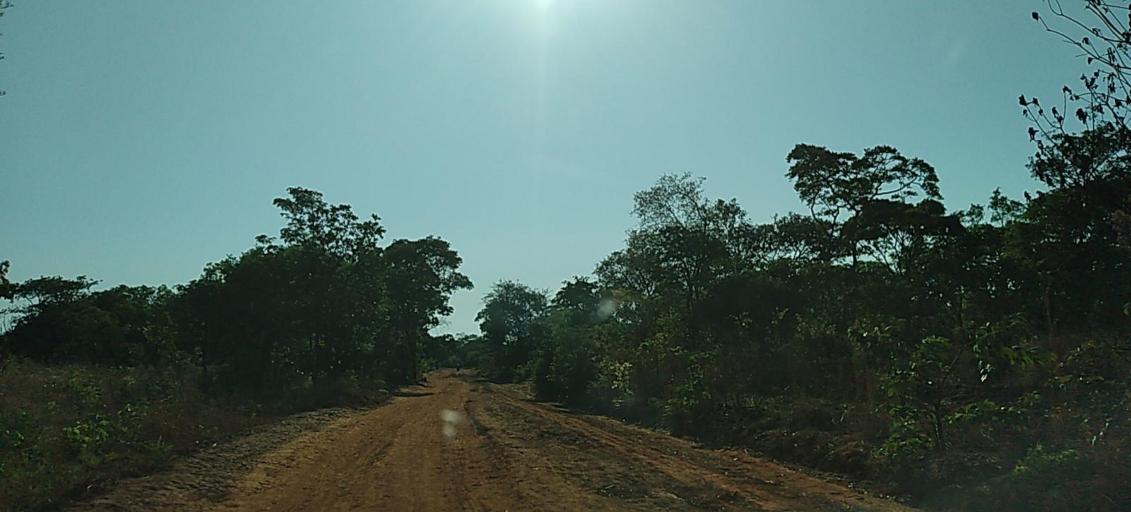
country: ZM
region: Copperbelt
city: Luanshya
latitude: -13.4592
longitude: 28.8126
